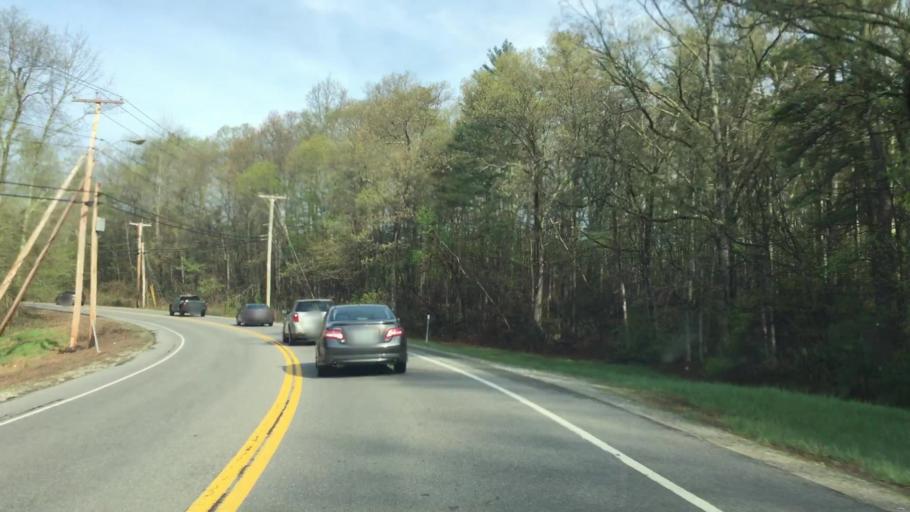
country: US
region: New Hampshire
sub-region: Hillsborough County
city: Pelham
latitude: 42.7050
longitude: -71.3670
